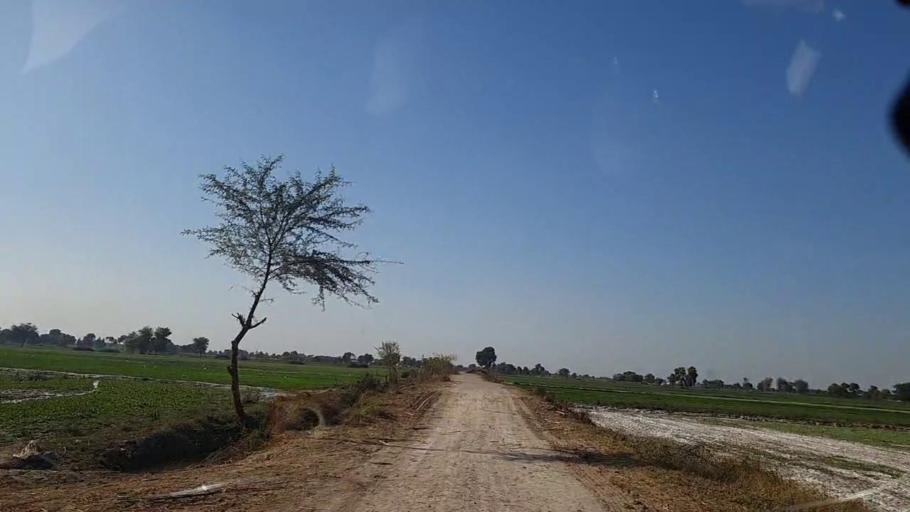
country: PK
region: Sindh
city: Khanpur
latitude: 27.7768
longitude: 69.3635
